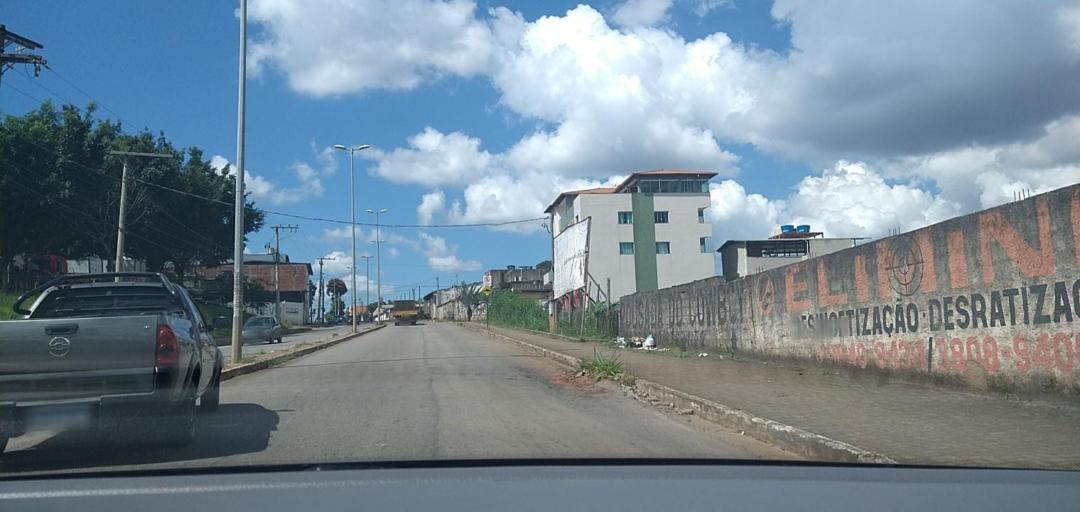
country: BR
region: Minas Gerais
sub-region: Joao Monlevade
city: Joao Monlevade
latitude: -19.8339
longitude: -43.1897
